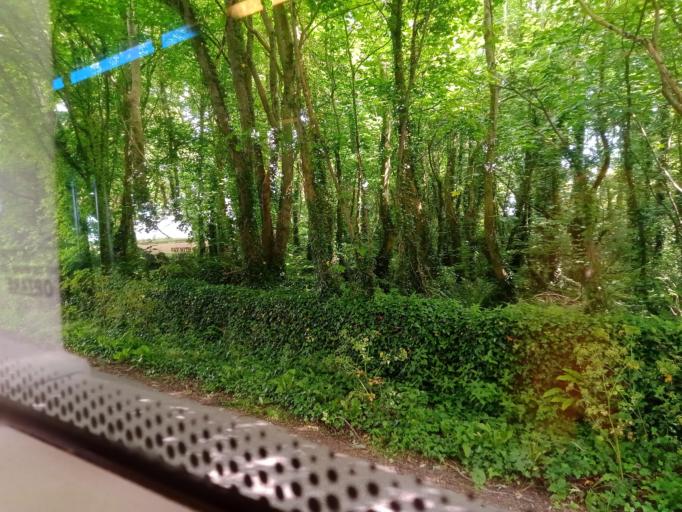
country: GB
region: Wales
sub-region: Anglesey
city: Beaumaris
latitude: 53.2663
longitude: -4.1136
